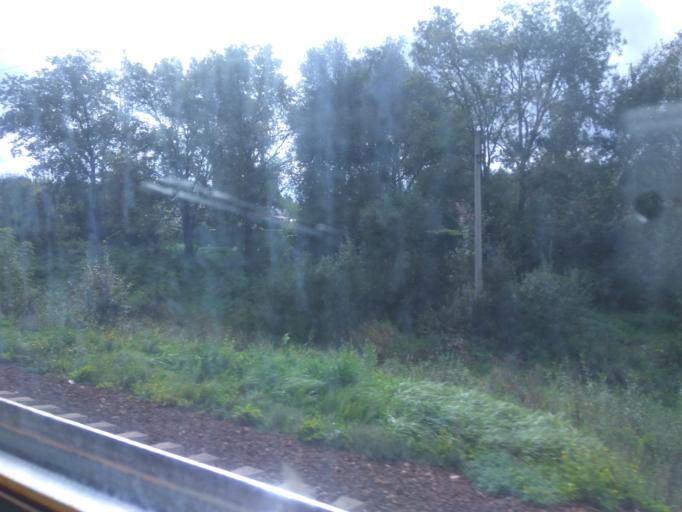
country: RU
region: Moskovskaya
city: Malyshevo
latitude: 55.4851
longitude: 38.3957
